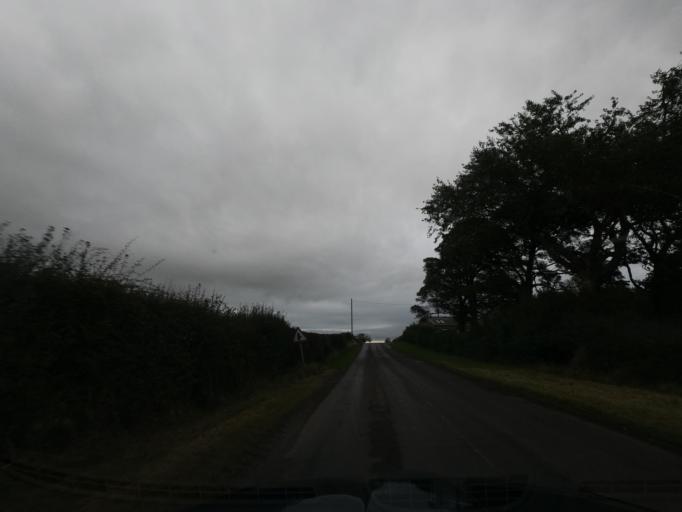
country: GB
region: England
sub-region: Northumberland
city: Ancroft
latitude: 55.7036
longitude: -2.0616
